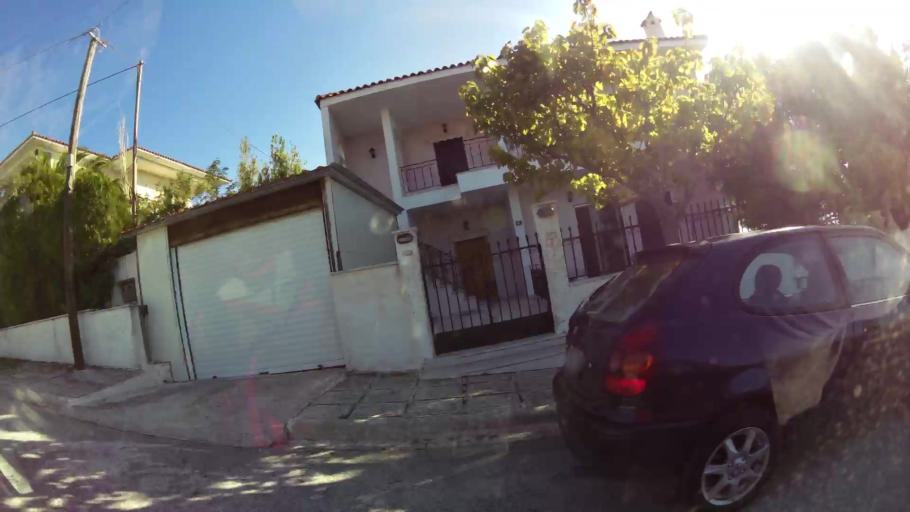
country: GR
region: Attica
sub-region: Nomarchia Anatolikis Attikis
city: Dhrafi
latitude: 38.0234
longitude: 23.9022
